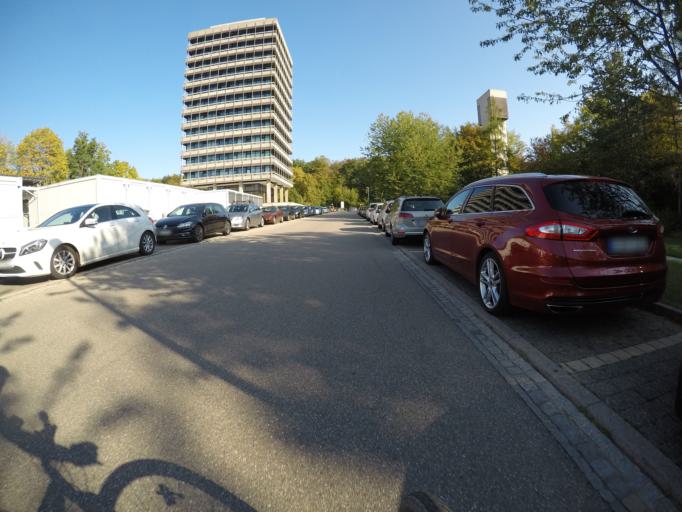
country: DE
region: Baden-Wuerttemberg
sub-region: Regierungsbezirk Stuttgart
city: Gerlingen
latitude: 48.7501
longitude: 9.1031
